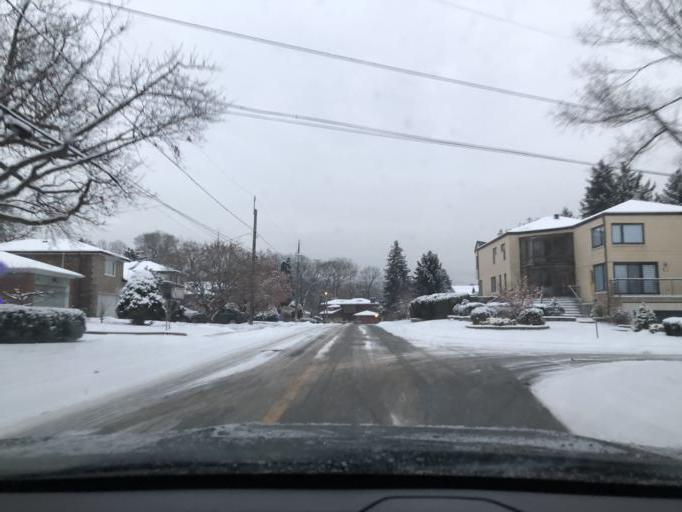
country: CA
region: Ontario
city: Toronto
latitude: 43.6977
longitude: -79.4838
